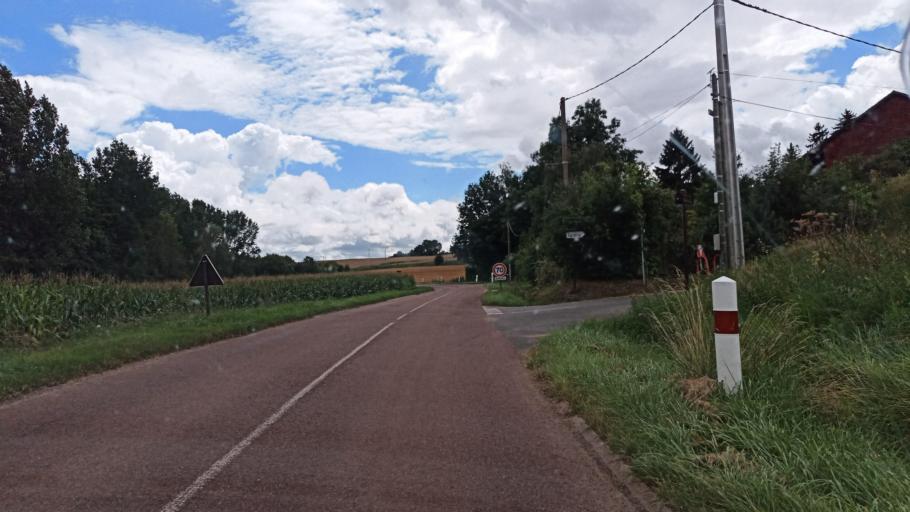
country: FR
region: Ile-de-France
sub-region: Departement de Seine-et-Marne
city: Voulx
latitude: 48.2697
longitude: 3.0003
